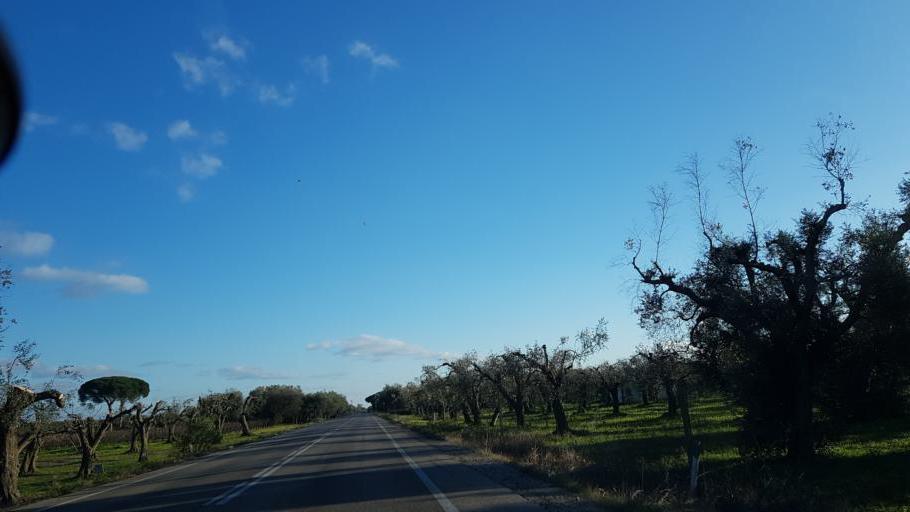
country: IT
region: Apulia
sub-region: Provincia di Lecce
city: Squinzano
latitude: 40.4564
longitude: 18.0239
